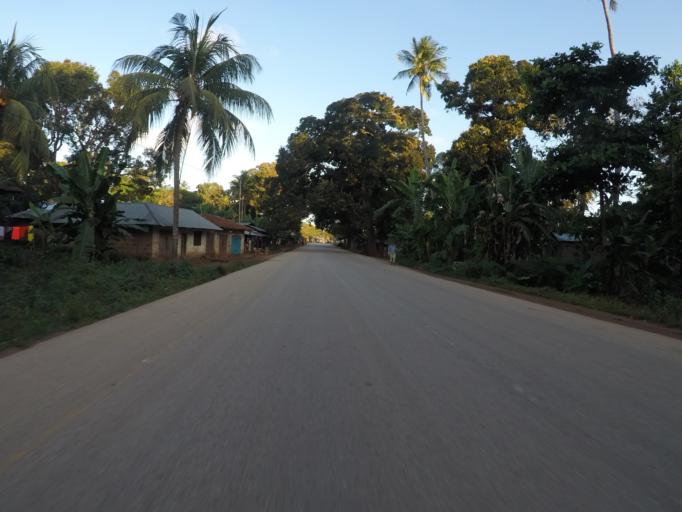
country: TZ
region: Zanzibar North
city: Gamba
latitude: -5.8837
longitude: 39.2848
